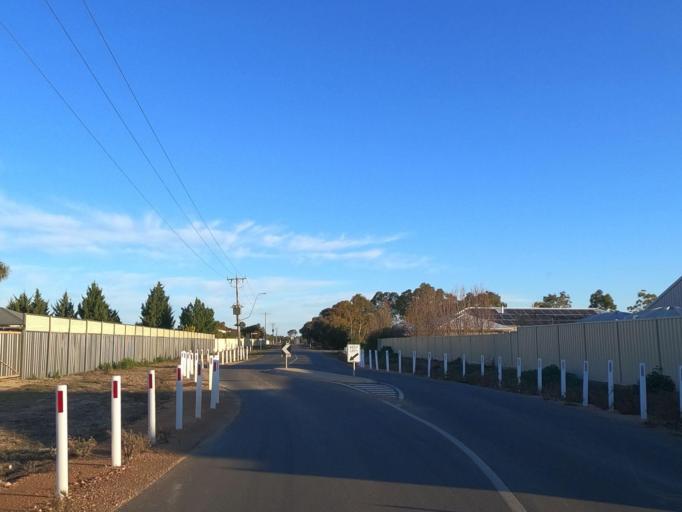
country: AU
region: Victoria
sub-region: Swan Hill
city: Swan Hill
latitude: -35.3291
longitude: 143.5348
